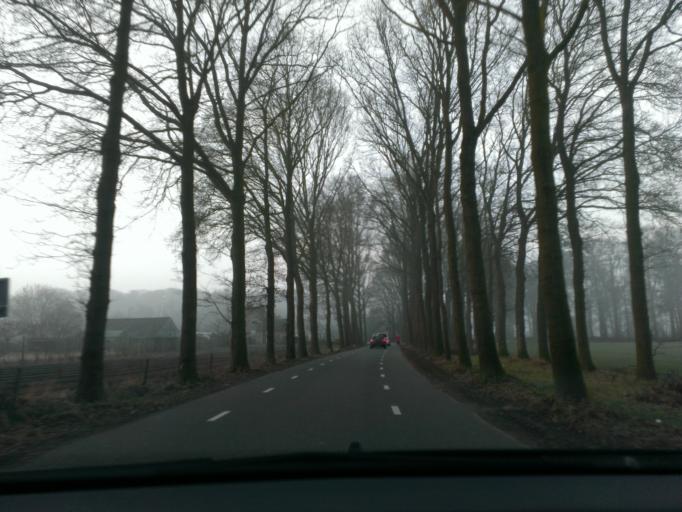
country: NL
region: Gelderland
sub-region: Gemeente Voorst
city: Twello
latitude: 52.2414
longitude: 6.0808
